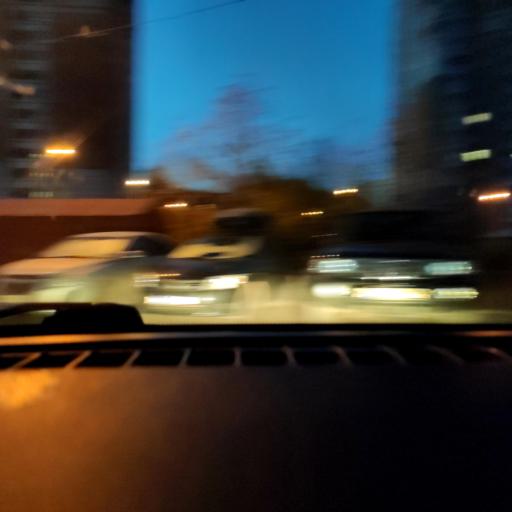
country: RU
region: Perm
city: Perm
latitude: 57.9643
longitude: 56.2123
